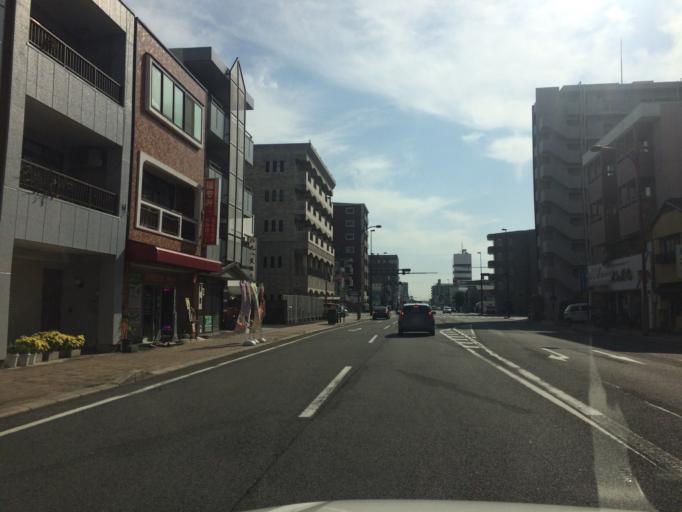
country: JP
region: Shizuoka
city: Shizuoka-shi
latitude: 34.9647
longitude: 138.3958
